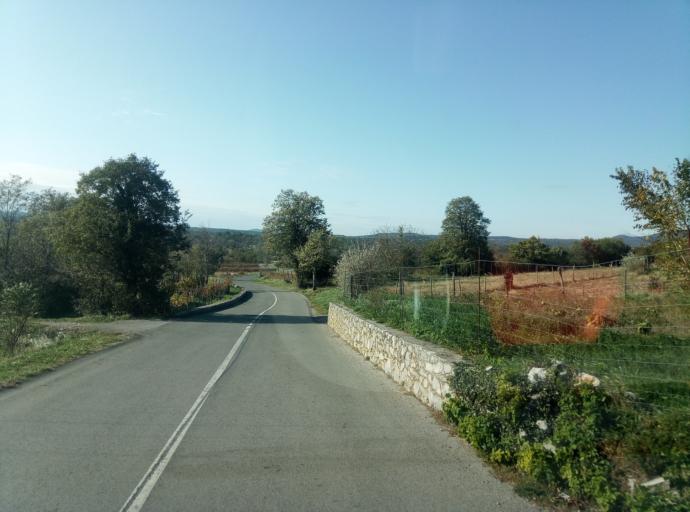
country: SI
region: Komen
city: Komen
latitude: 45.8145
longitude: 13.8070
